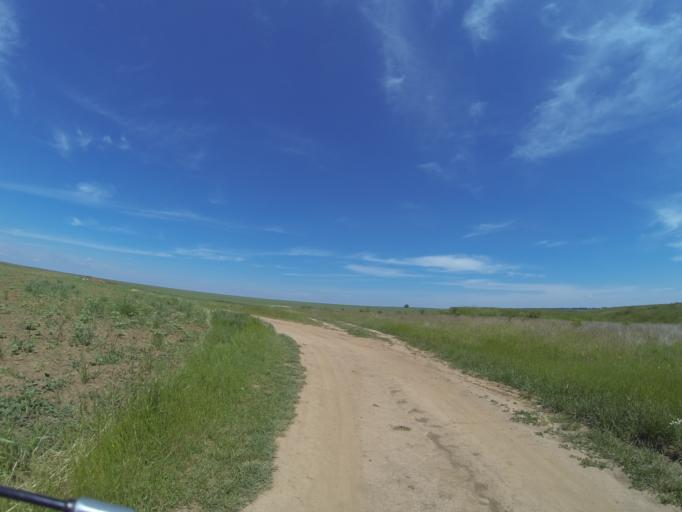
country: RO
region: Dolj
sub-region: Comuna Teslui
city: Teslui
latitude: 44.1791
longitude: 24.1709
